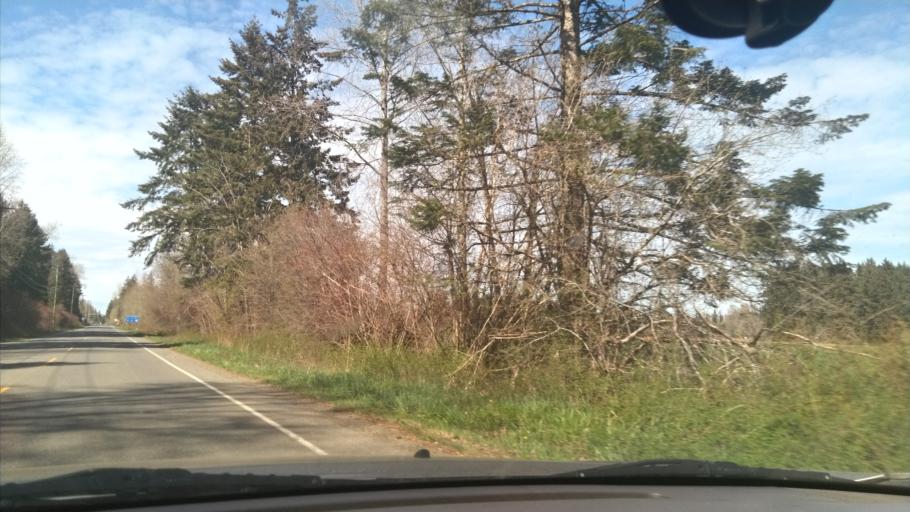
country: CA
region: British Columbia
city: Courtenay
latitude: 49.7031
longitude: -125.0212
